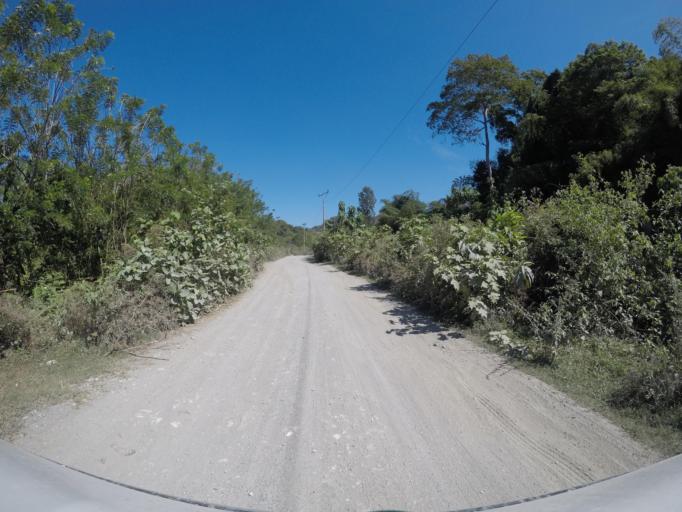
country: TL
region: Manufahi
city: Same
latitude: -8.9588
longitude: 126.0089
